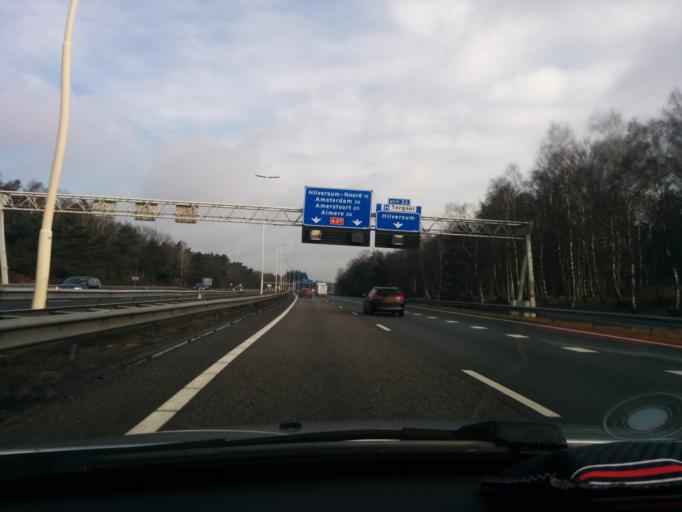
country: NL
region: North Holland
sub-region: Gemeente Hilversum
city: Hilversum
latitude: 52.1874
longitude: 5.1853
